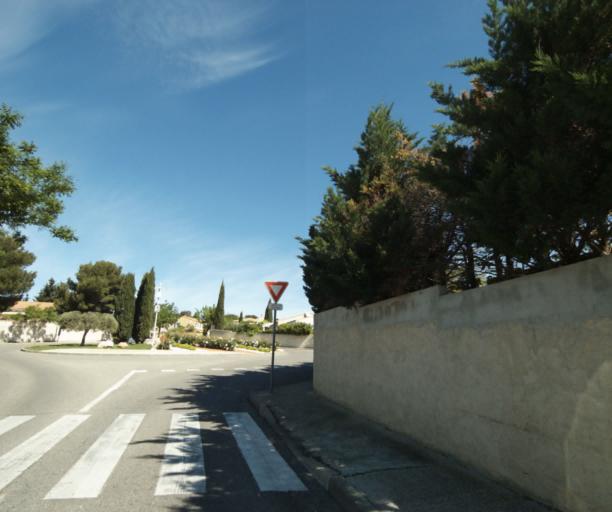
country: FR
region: Provence-Alpes-Cote d'Azur
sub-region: Departement des Bouches-du-Rhone
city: Rognac
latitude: 43.5093
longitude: 5.2140
